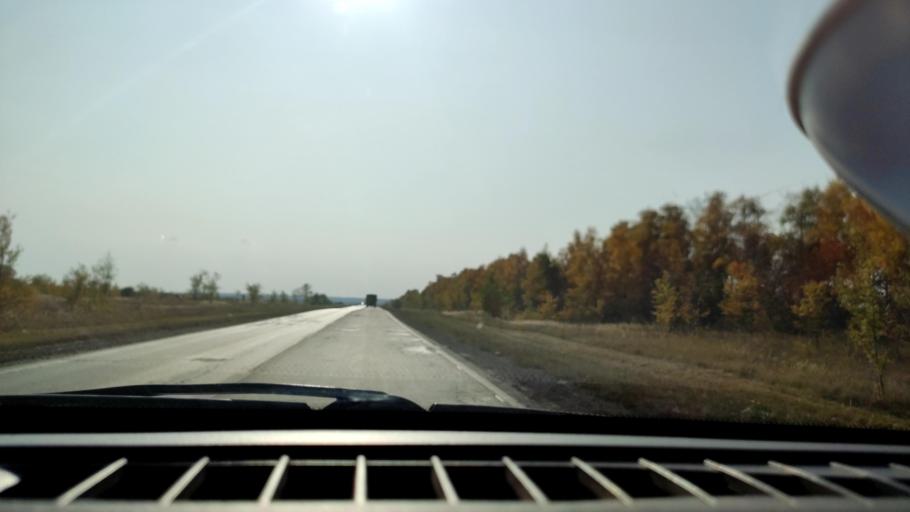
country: RU
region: Samara
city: Smyshlyayevka
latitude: 53.1164
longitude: 50.3616
